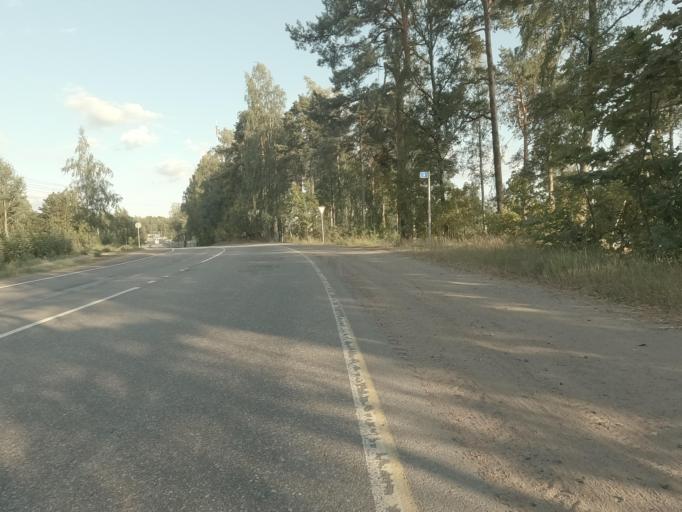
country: RU
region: Leningrad
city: Vyborg
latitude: 60.7265
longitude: 28.7604
